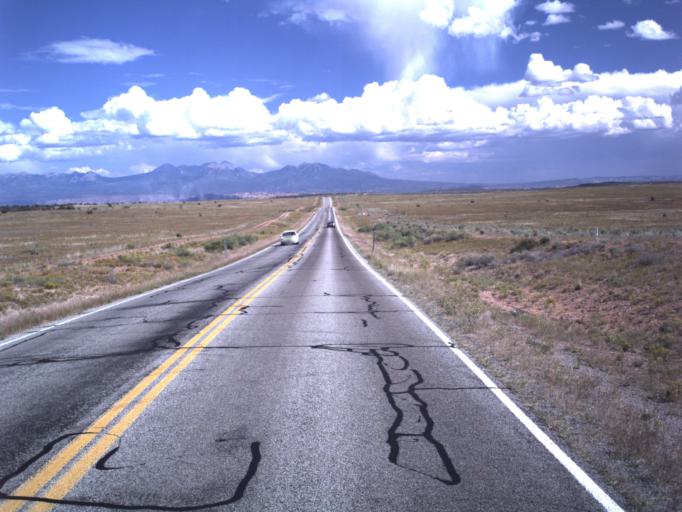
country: US
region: Utah
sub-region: Grand County
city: Moab
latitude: 38.5507
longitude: -109.7834
